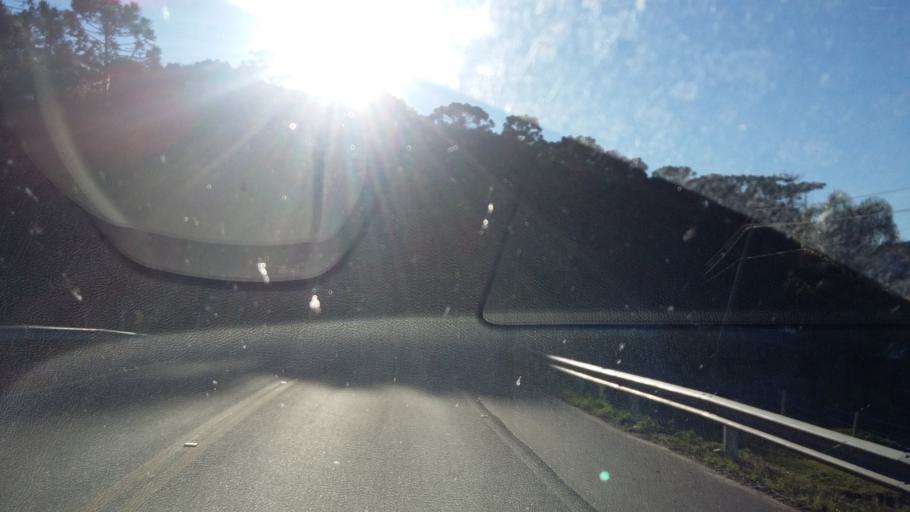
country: BR
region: Santa Catarina
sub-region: Lauro Muller
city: Lauro Muller
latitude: -28.0102
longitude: -49.5352
